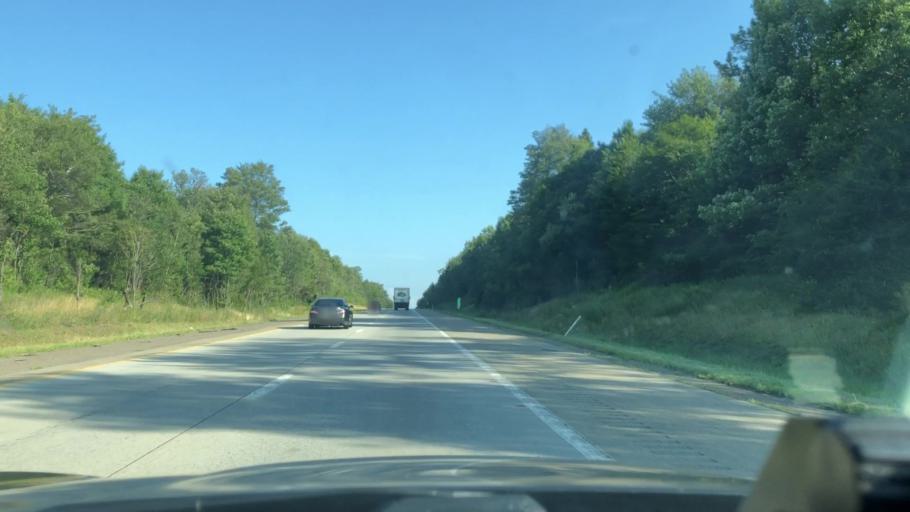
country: US
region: Pennsylvania
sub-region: Monroe County
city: Pocono Pines
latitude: 41.1604
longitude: -75.4183
